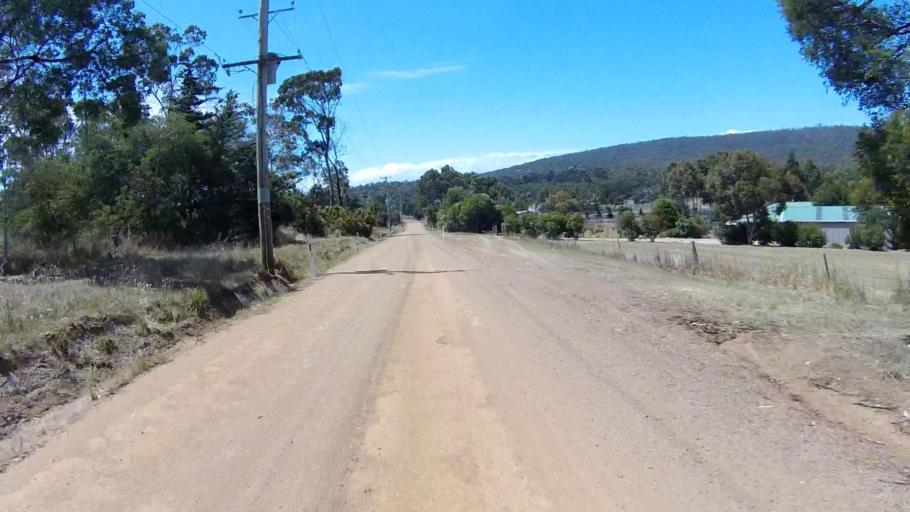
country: AU
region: Tasmania
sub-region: Clarence
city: Sandford
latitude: -42.9664
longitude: 147.4698
